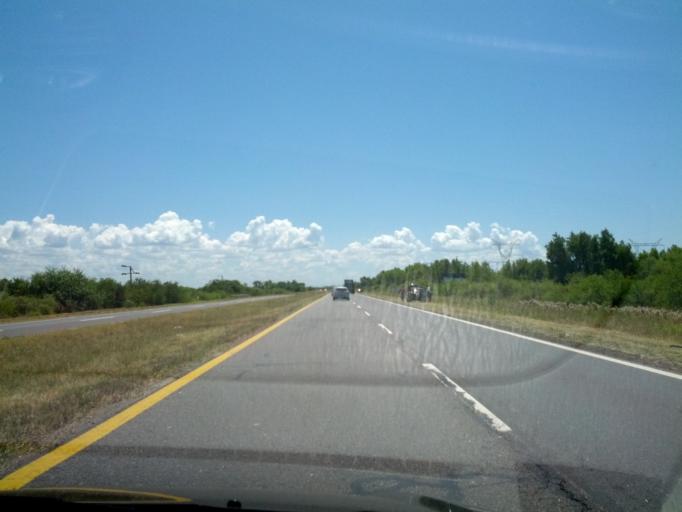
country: AR
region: Entre Rios
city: Villa Paranacito
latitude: -33.7624
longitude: -58.8638
